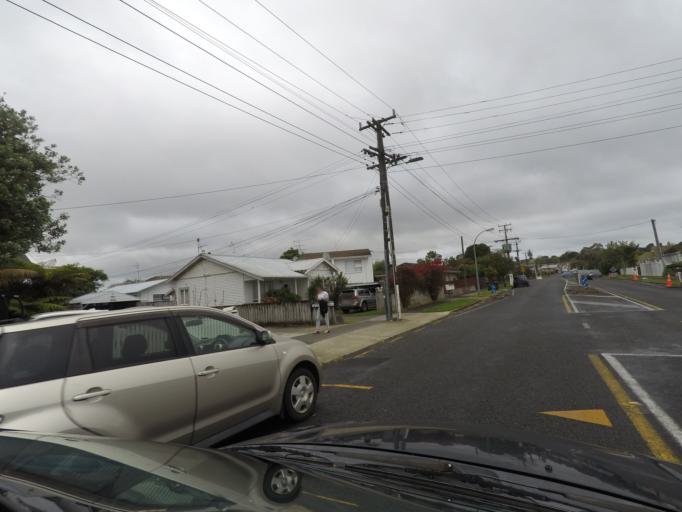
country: NZ
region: Auckland
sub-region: Auckland
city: Auckland
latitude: -36.8886
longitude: 174.7324
